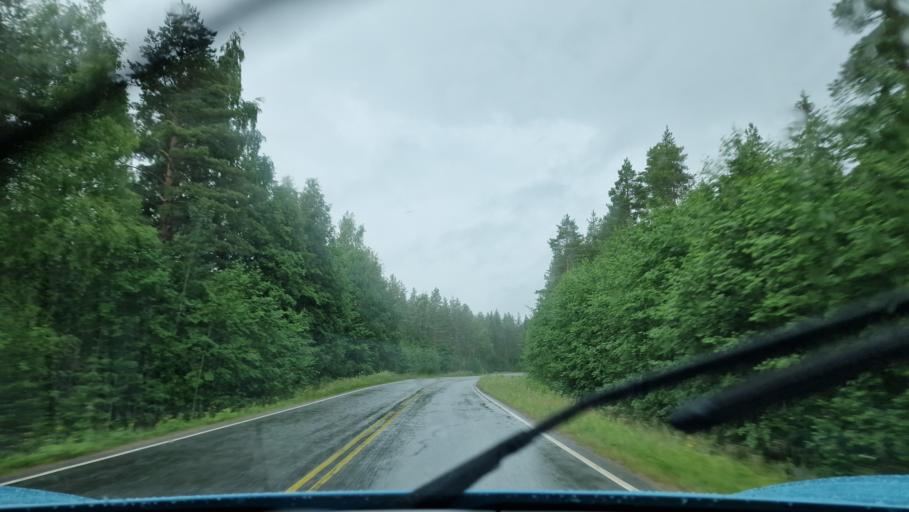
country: FI
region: Southern Ostrobothnia
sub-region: Jaerviseutu
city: Soini
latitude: 62.8180
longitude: 24.3519
